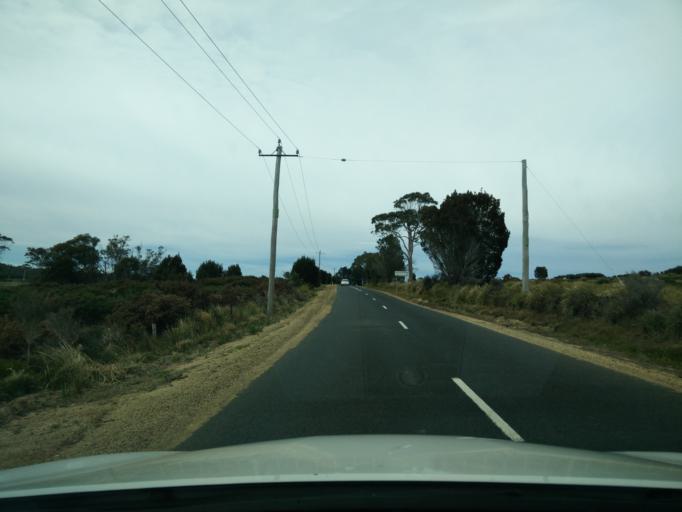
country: AU
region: Tasmania
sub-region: Break O'Day
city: St Helens
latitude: -41.9306
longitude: 148.2276
